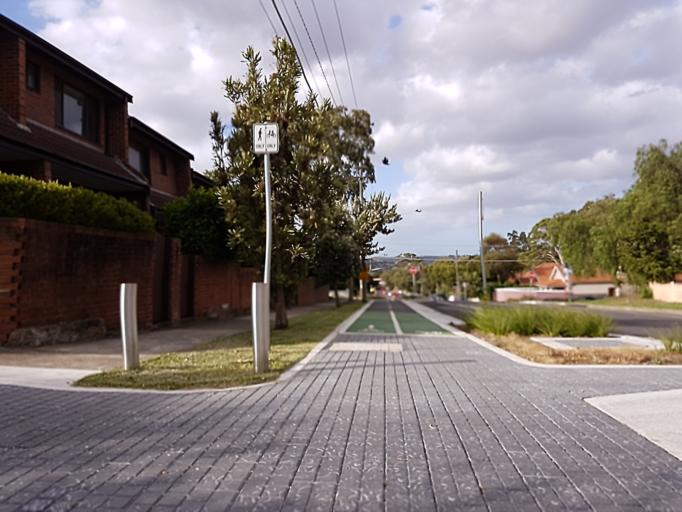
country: AU
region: New South Wales
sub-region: North Sydney
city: Cremorne
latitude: -33.8274
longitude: 151.2225
